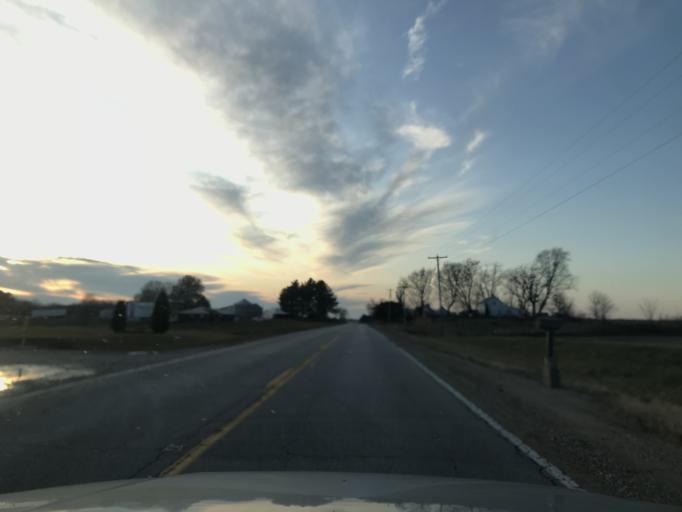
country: US
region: Illinois
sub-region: Warren County
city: Monmouth
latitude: 41.0250
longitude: -90.7685
